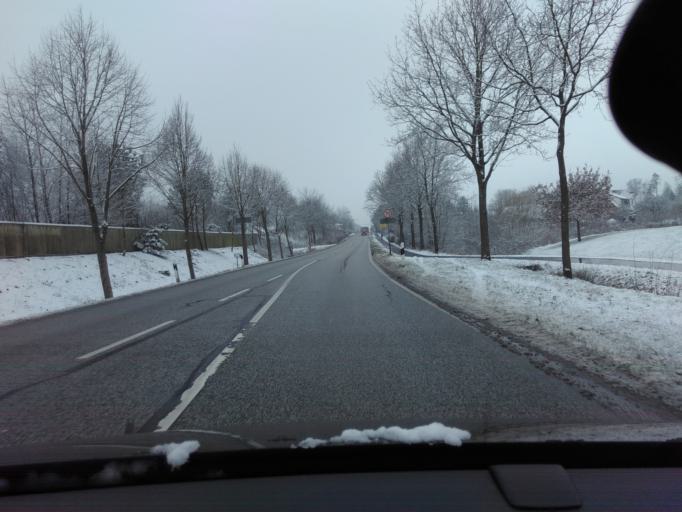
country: DE
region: Schleswig-Holstein
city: Ahrensbok
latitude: 54.0187
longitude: 10.5773
